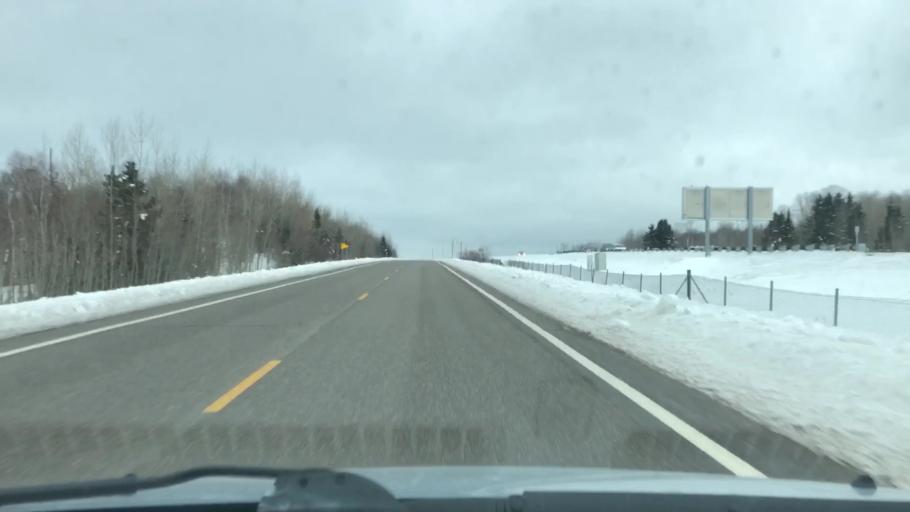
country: US
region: Minnesota
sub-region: Saint Louis County
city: Proctor
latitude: 46.7185
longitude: -92.2440
